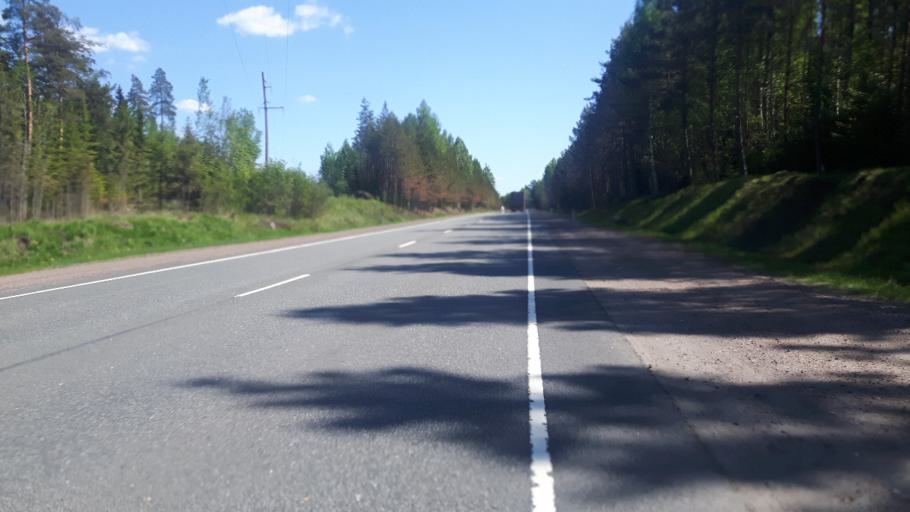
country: FI
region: South Karelia
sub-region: Lappeenranta
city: Ylaemaa
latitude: 60.6262
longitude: 28.2264
